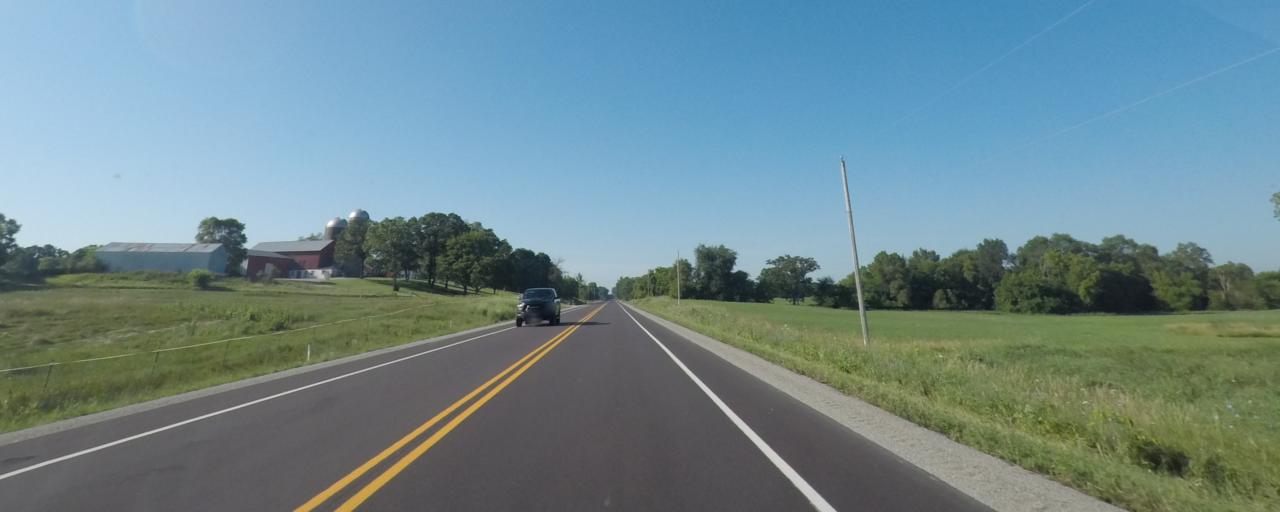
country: US
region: Wisconsin
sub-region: Jefferson County
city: Palmyra
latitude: 42.9252
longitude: -88.5864
